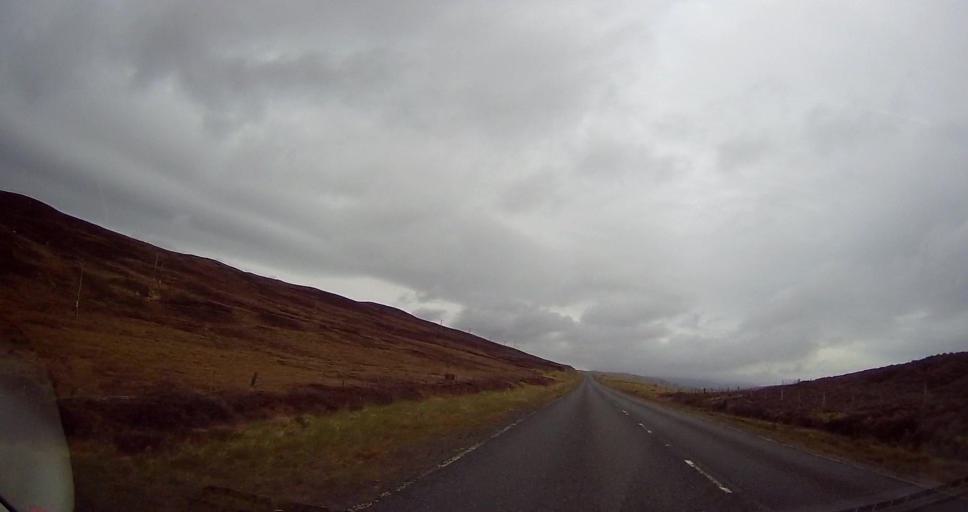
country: GB
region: Scotland
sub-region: Shetland Islands
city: Lerwick
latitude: 60.2110
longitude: -1.2333
